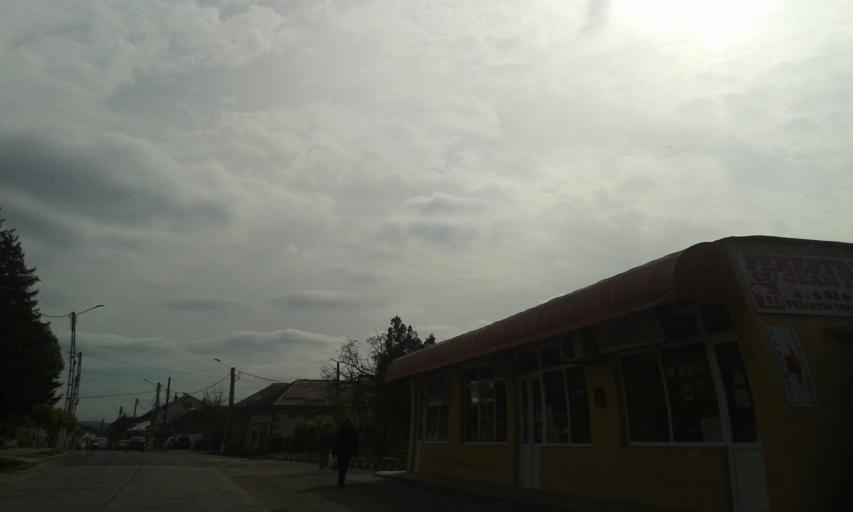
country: RO
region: Gorj
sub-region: Comuna Targu Carbunesti
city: Targu Carbunesti
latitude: 44.9580
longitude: 23.5114
